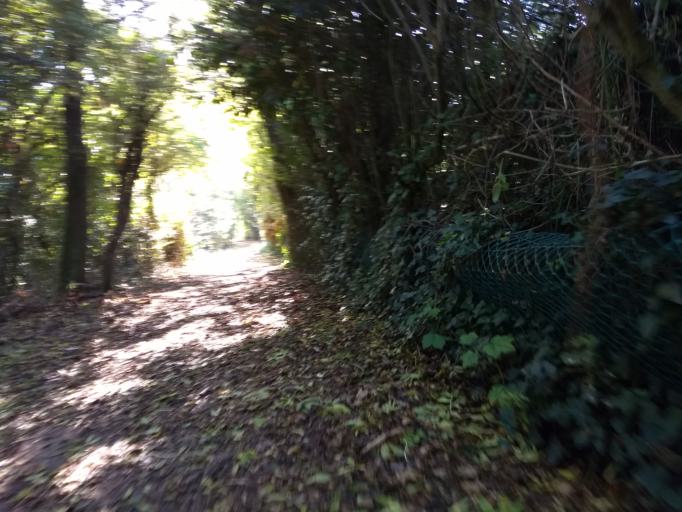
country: GB
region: England
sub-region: Isle of Wight
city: Ventnor
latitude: 50.6197
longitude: -1.2240
